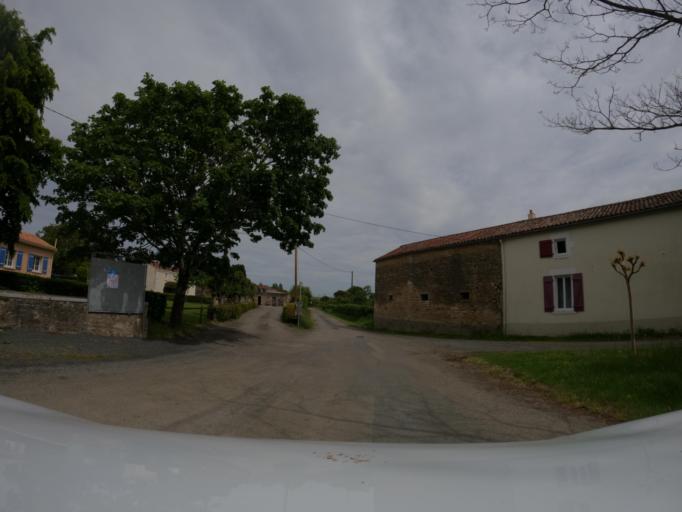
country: FR
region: Pays de la Loire
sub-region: Departement de la Vendee
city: Saint-Hilaire-des-Loges
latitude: 46.4907
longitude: -0.6331
